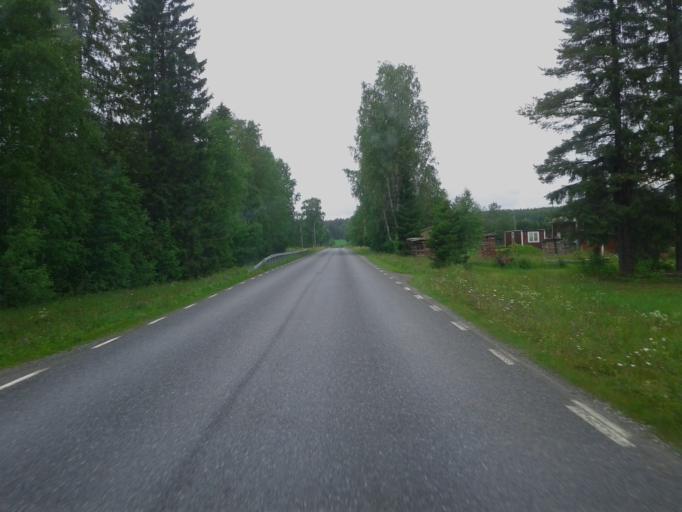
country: SE
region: Vaesterbotten
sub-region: Skelleftea Kommun
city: Forsbacka
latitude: 64.9012
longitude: 20.6576
